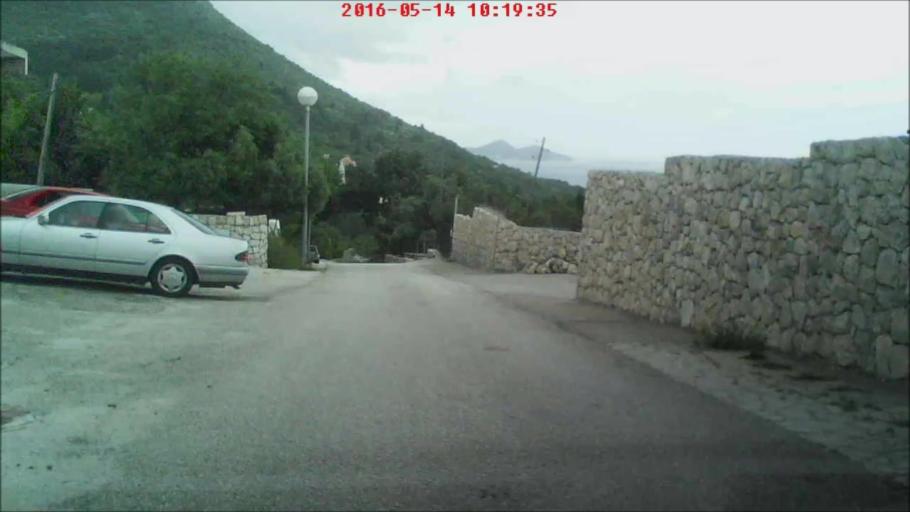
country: HR
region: Dubrovacko-Neretvanska
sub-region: Grad Dubrovnik
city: Mokosica
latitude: 42.7164
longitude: 17.9710
